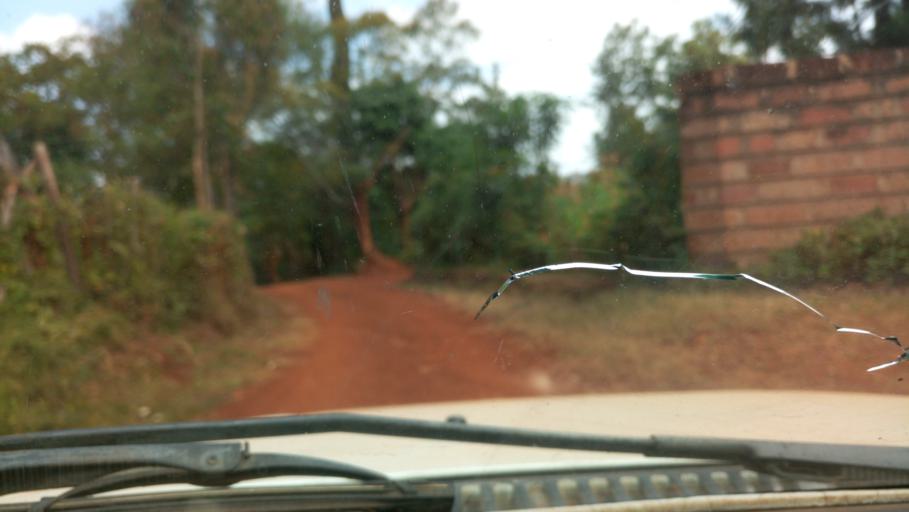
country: KE
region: Murang'a District
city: Maragua
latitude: -0.7653
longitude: 37.1034
